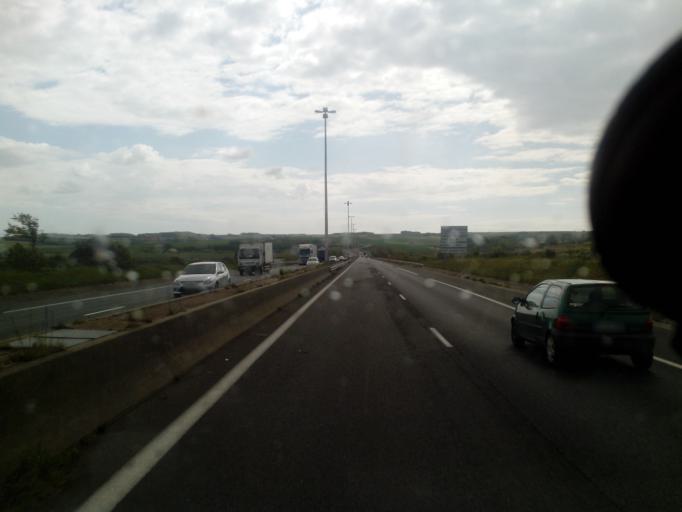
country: FR
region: Nord-Pas-de-Calais
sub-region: Departement du Pas-de-Calais
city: Coquelles
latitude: 50.9225
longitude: 1.7980
